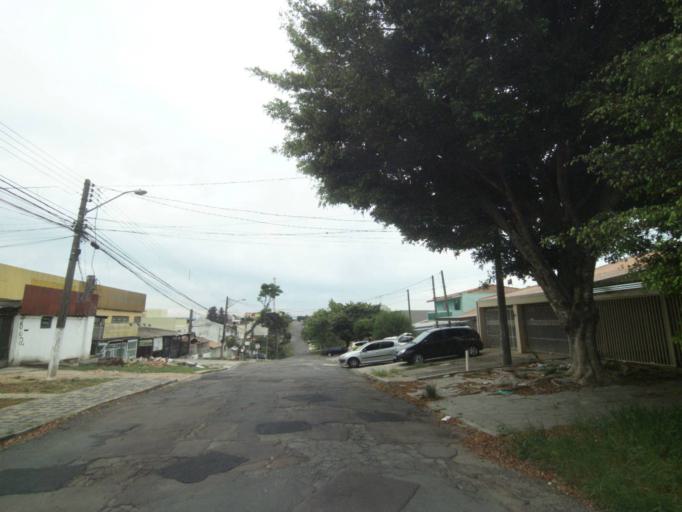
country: BR
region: Parana
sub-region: Pinhais
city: Pinhais
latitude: -25.4186
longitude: -49.2060
